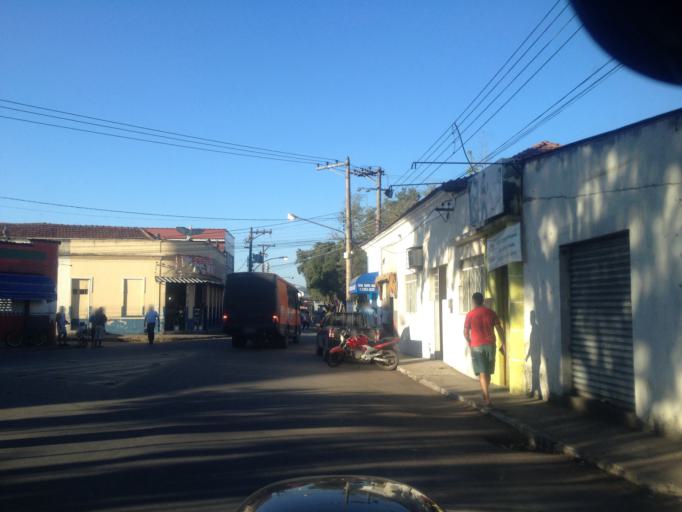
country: BR
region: Rio de Janeiro
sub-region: Quatis
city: Quatis
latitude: -22.4099
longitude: -44.2616
